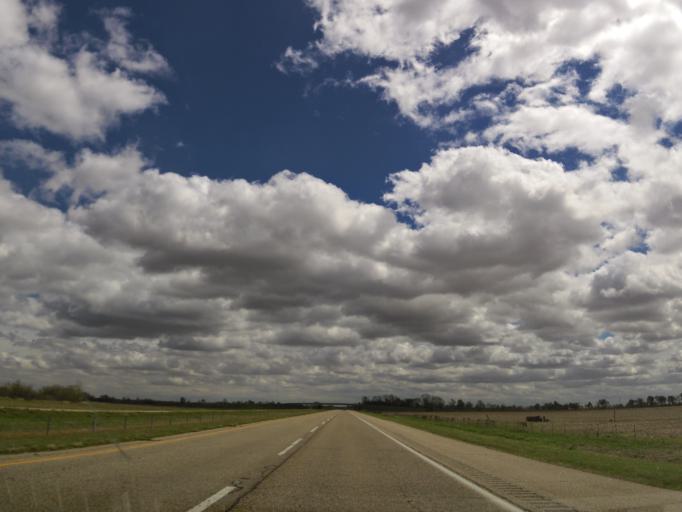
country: US
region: Arkansas
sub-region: Poinsett County
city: Trumann
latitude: 35.6574
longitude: -90.5427
